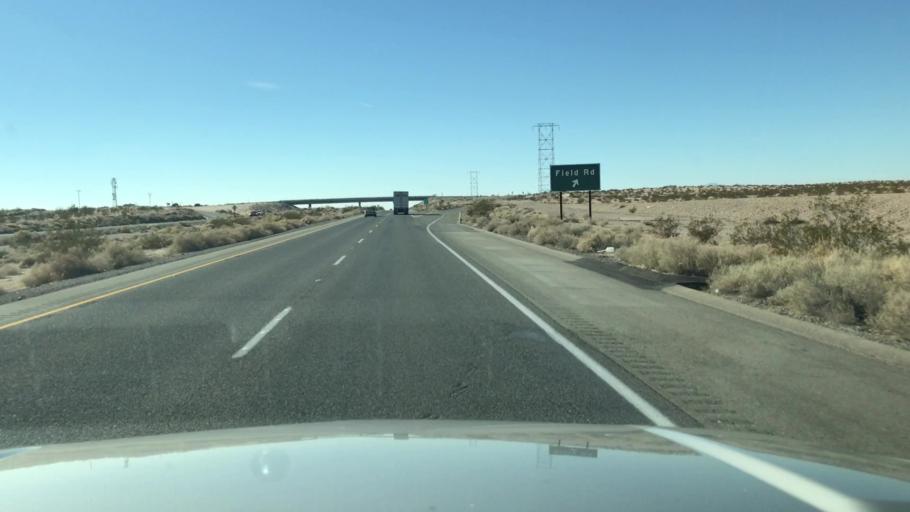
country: US
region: California
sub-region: San Bernardino County
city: Fort Irwin
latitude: 35.0129
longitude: -116.5266
